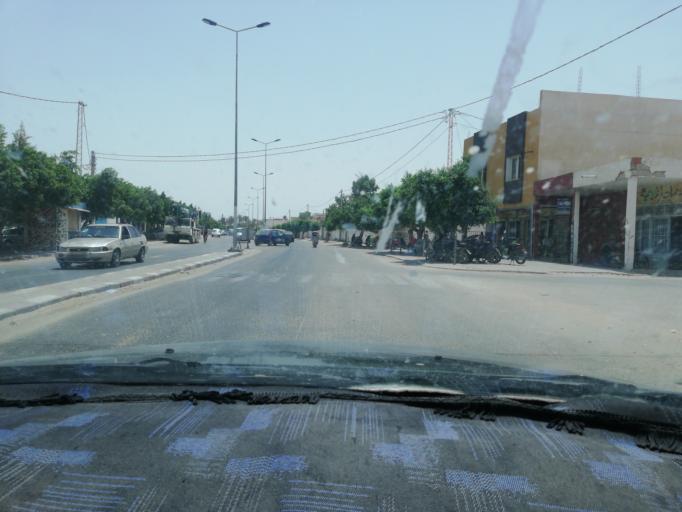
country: TN
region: Qabis
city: Gabes
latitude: 33.6204
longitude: 10.2834
